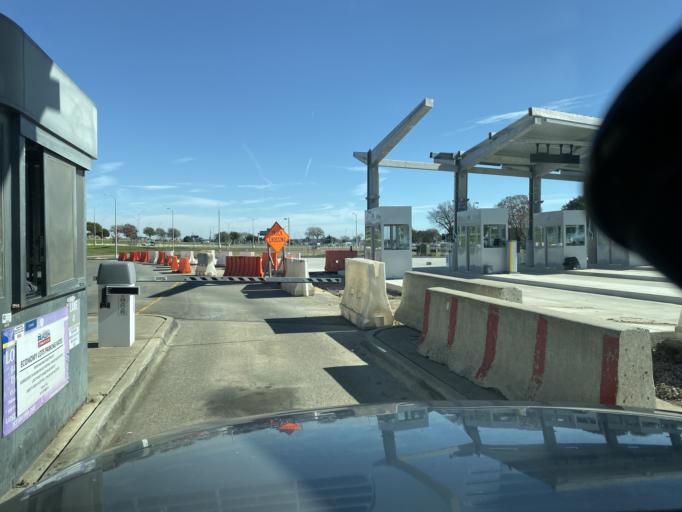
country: US
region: Texas
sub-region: Travis County
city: Hornsby Bend
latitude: 30.2091
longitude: -97.6662
